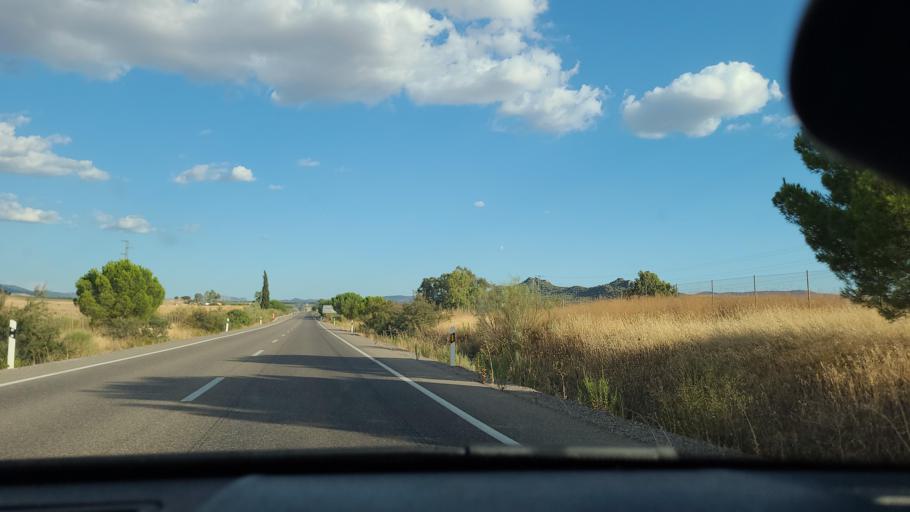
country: ES
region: Andalusia
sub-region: Province of Cordoba
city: Belmez
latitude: 38.2708
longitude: -5.1924
